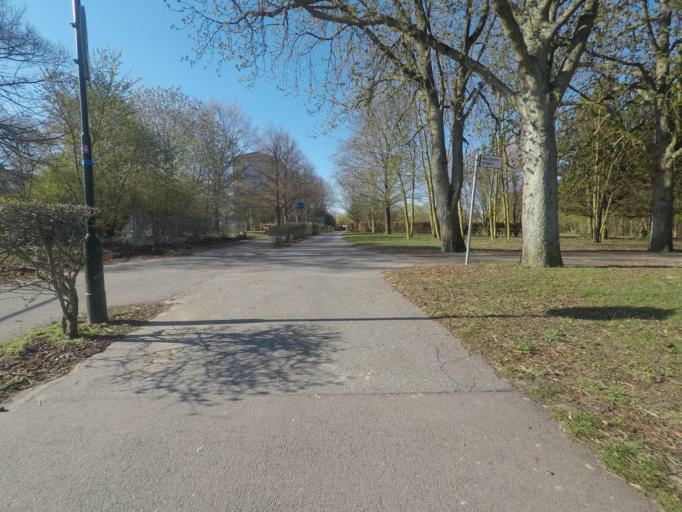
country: SE
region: Skane
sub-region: Malmo
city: Malmoe
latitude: 55.5679
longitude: 13.0171
